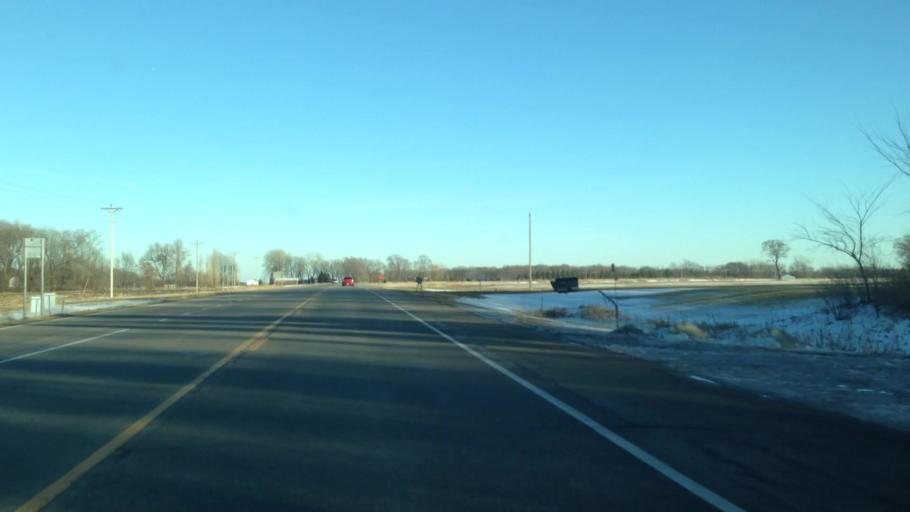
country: US
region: Minnesota
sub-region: Scott County
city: Elko New Market
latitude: 44.4792
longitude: -93.3211
